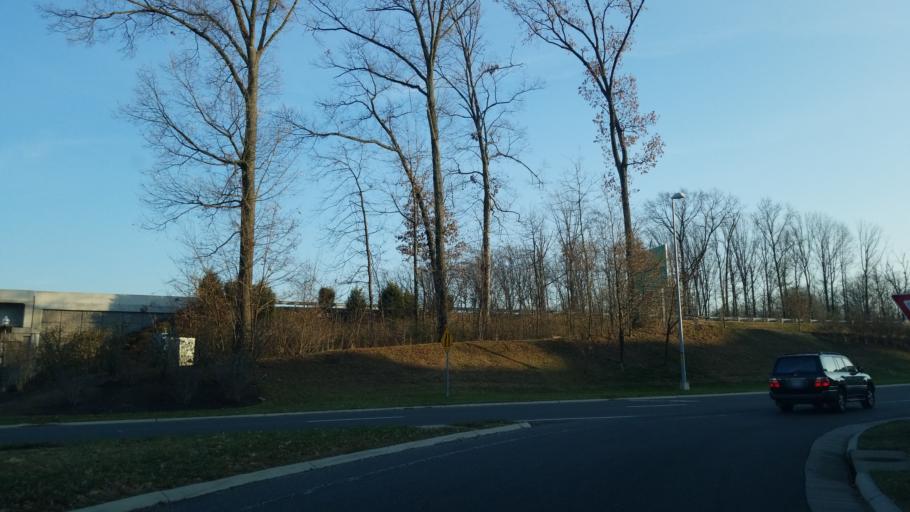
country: US
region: Virginia
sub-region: Fairfax County
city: Greenbriar
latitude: 38.8629
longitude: -77.3832
